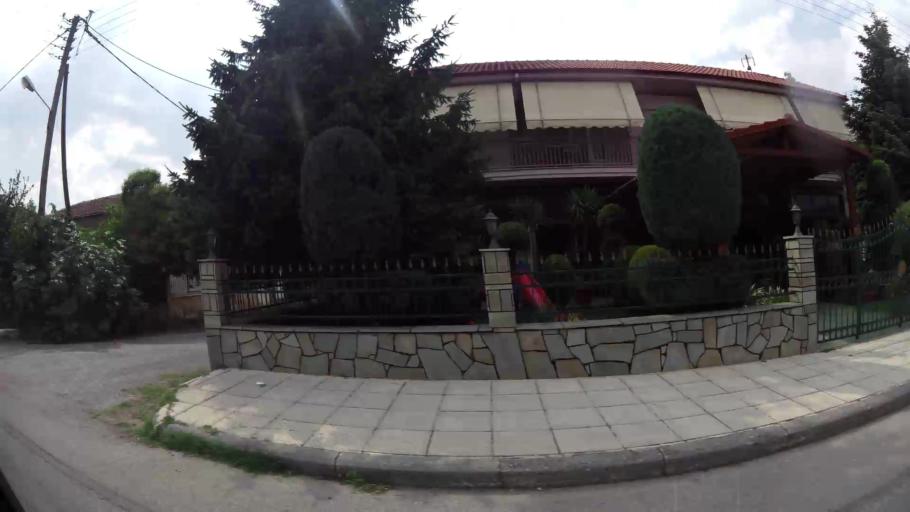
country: GR
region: West Macedonia
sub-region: Nomos Kozanis
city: Koila
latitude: 40.3467
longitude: 21.8270
